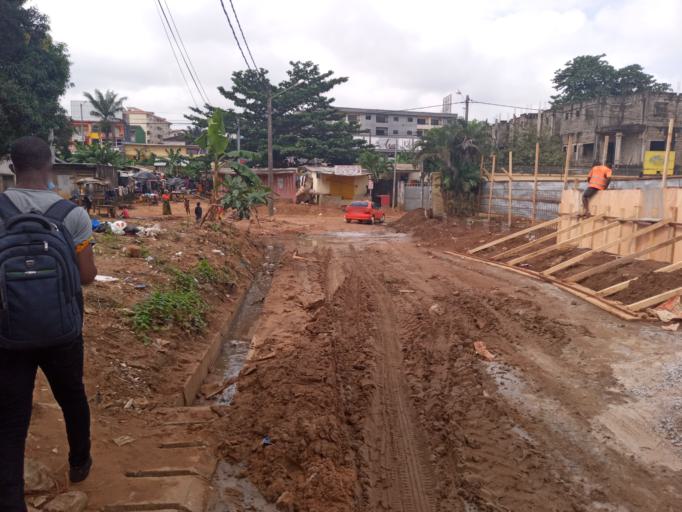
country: CI
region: Lagunes
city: Bingerville
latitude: 5.3644
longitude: -3.9554
